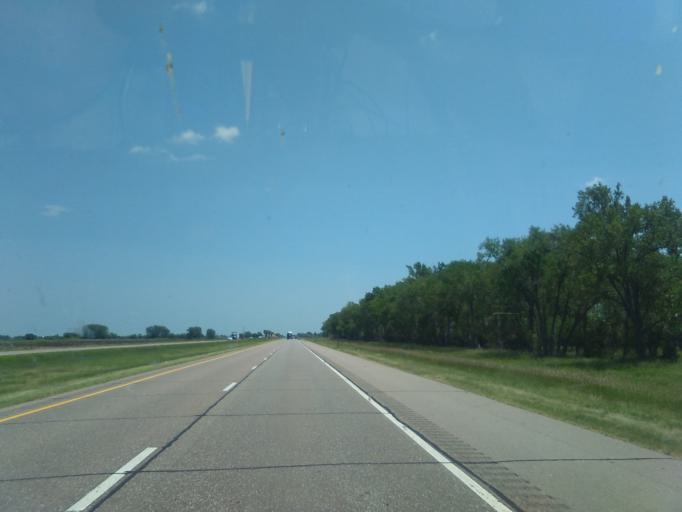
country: US
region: Nebraska
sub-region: Dawson County
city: Cozad
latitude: 40.8761
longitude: -100.0622
